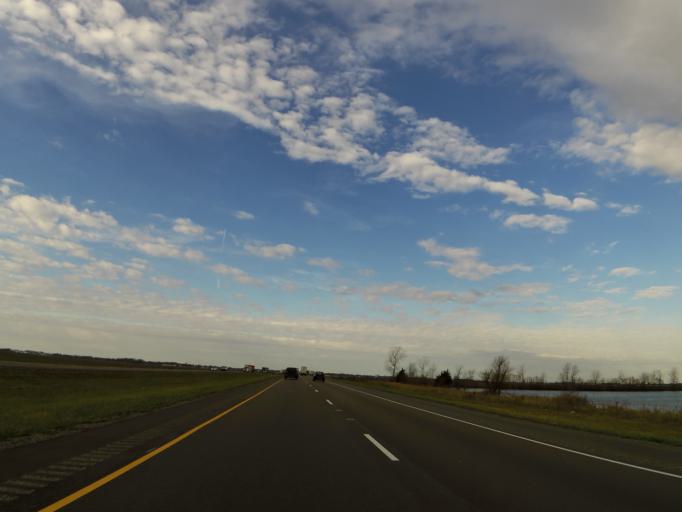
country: US
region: Illinois
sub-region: Washington County
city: Okawville
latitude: 38.4276
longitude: -89.4793
